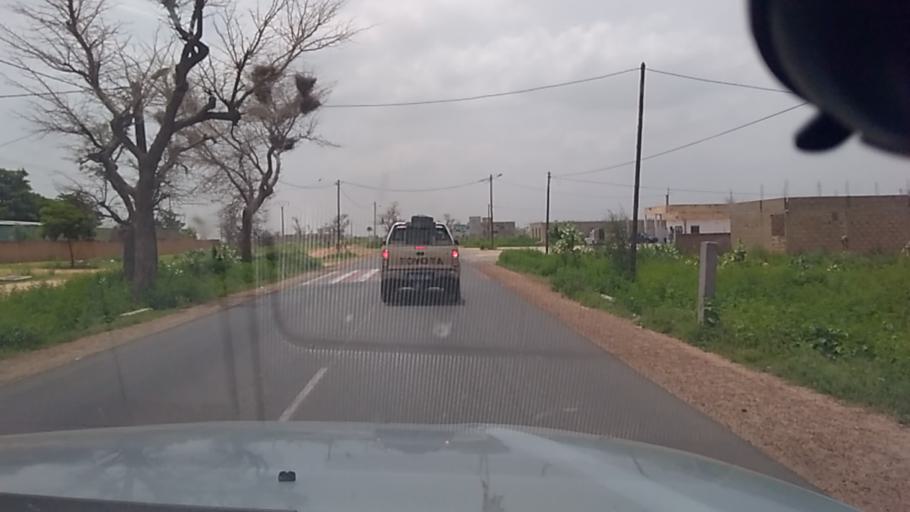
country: SN
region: Thies
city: Mekhe
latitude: 15.0077
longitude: -16.7433
